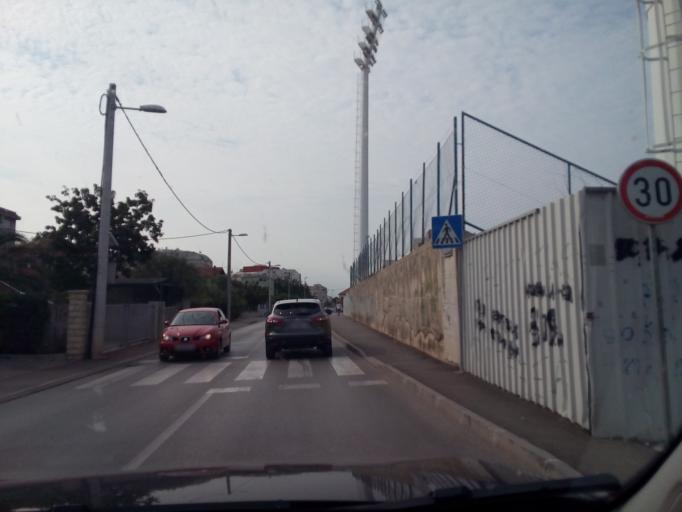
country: HR
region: Zadarska
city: Zadar
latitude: 44.1134
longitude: 15.2470
